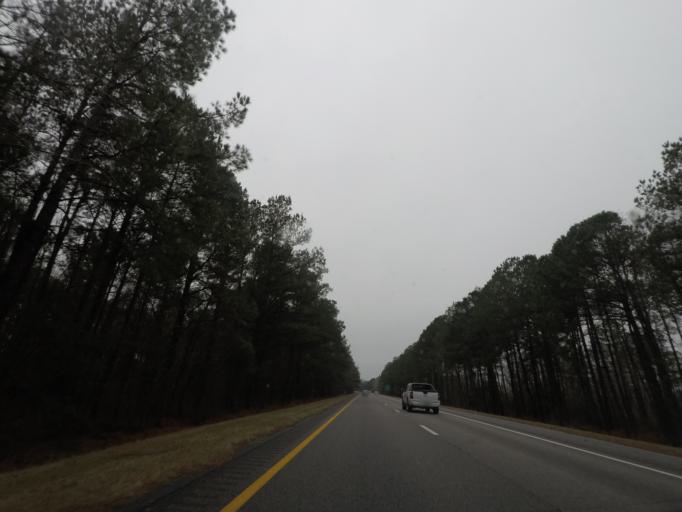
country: US
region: South Carolina
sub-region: Sumter County
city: East Sumter
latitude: 33.9180
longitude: -80.0815
